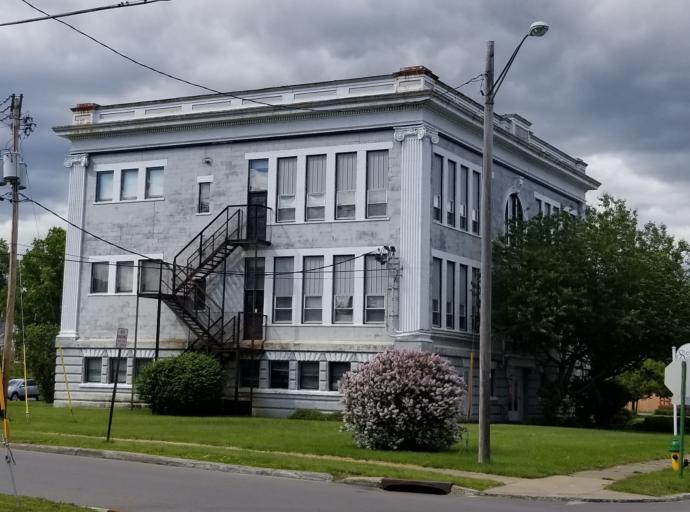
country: US
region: New York
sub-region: Herkimer County
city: Herkimer
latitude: 43.0336
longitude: -74.9880
